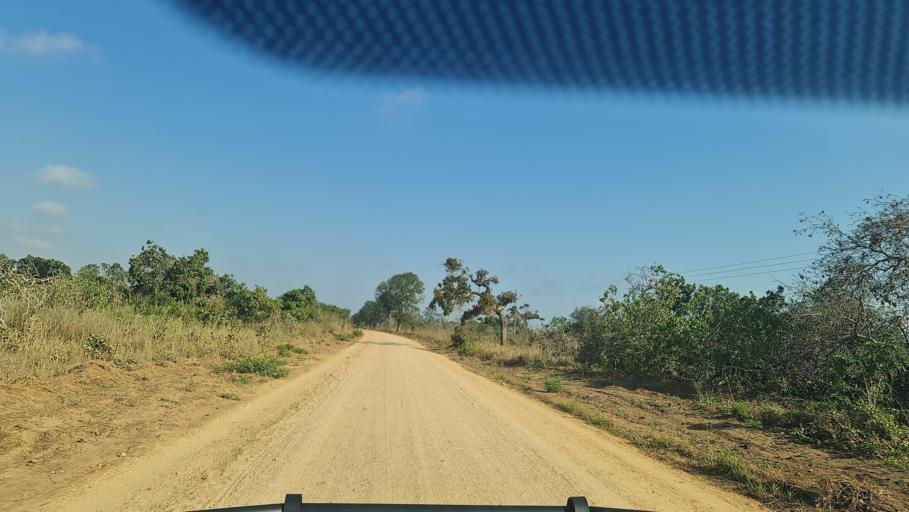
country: MZ
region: Nampula
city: Ilha de Mocambique
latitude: -15.3015
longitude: 40.1286
